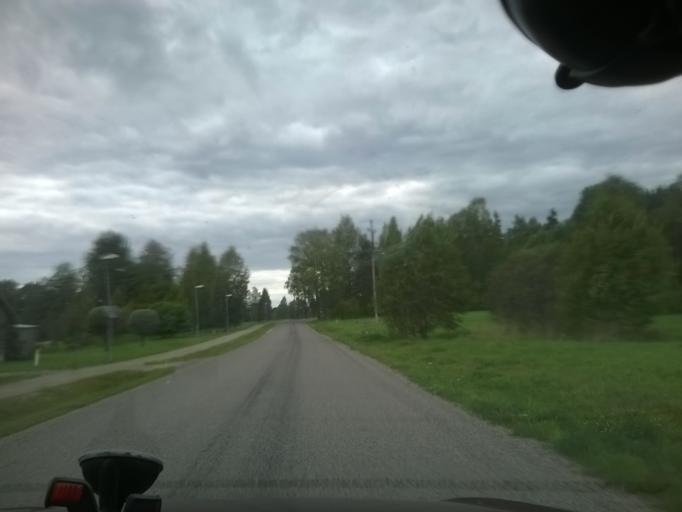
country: EE
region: Vorumaa
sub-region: Voru linn
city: Voru
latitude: 57.7304
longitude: 26.9359
